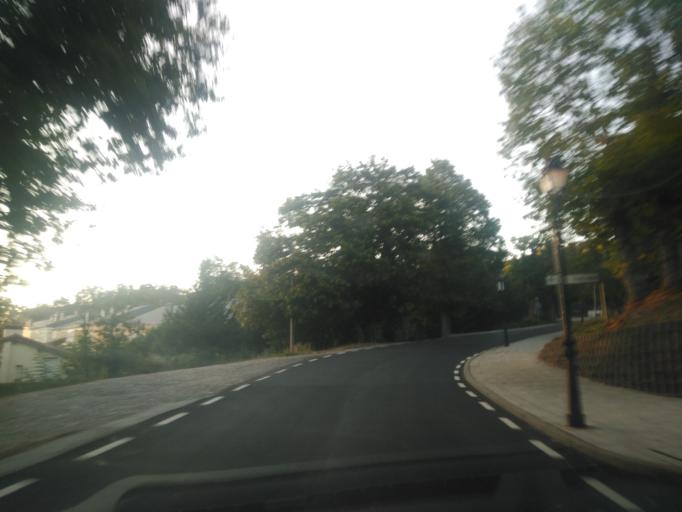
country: ES
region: Castille and Leon
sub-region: Provincia de Salamanca
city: Bejar
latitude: 40.3797
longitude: -5.7640
